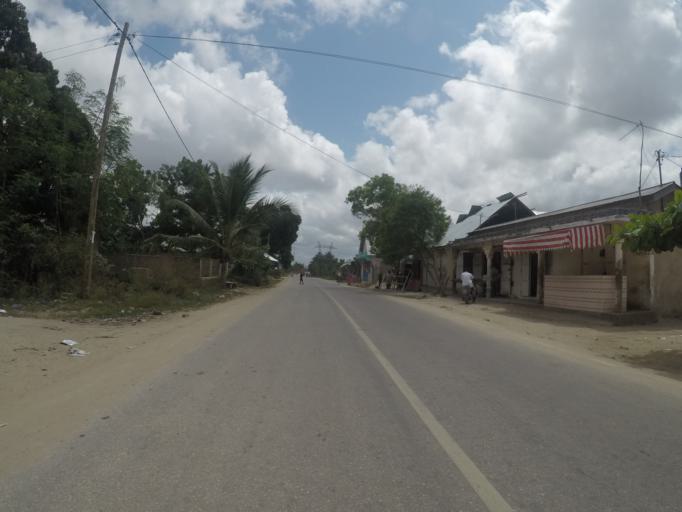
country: TZ
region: Zanzibar Urban/West
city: Zanzibar
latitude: -6.2042
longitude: 39.2433
